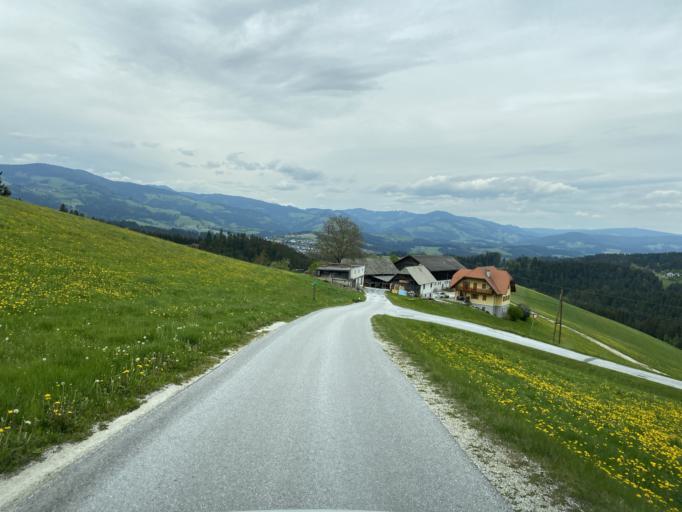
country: AT
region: Styria
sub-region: Politischer Bezirk Weiz
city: Gschaid bei Birkfeld
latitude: 47.3367
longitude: 15.7296
